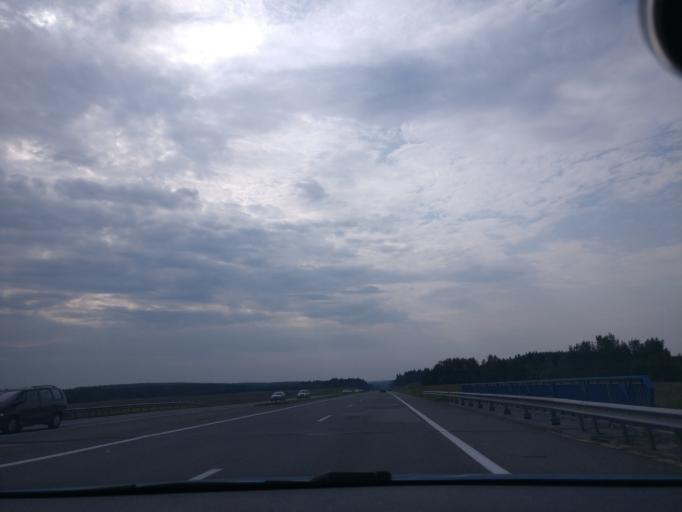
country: BY
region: Minsk
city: Lahoysk
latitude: 54.1478
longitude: 27.8098
